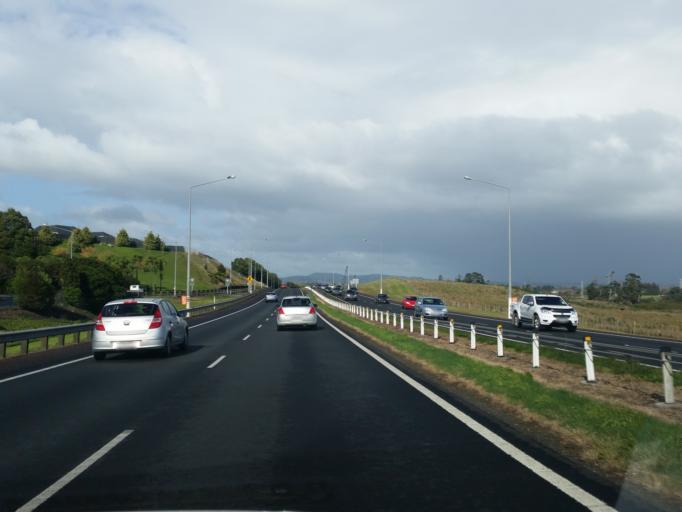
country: NZ
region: Auckland
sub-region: Auckland
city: Papakura
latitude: -37.0885
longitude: 174.9392
